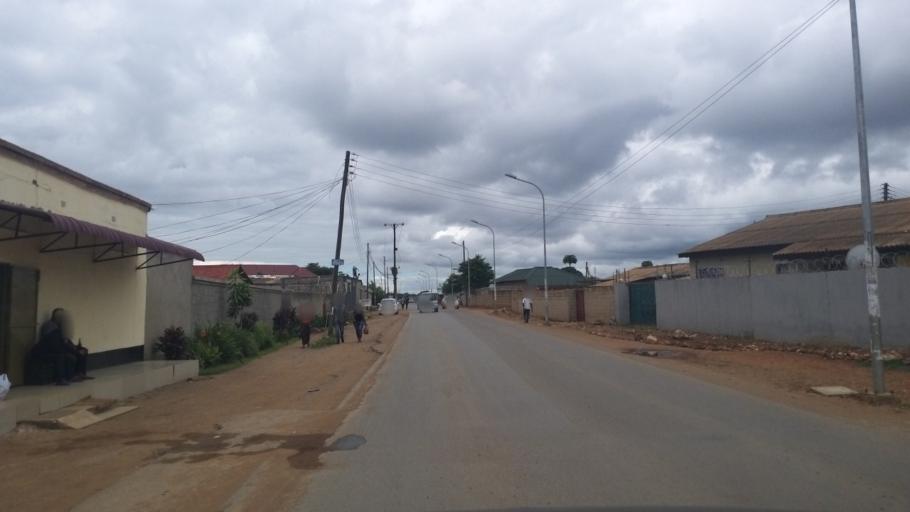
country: ZM
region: Lusaka
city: Lusaka
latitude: -15.4451
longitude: 28.3057
